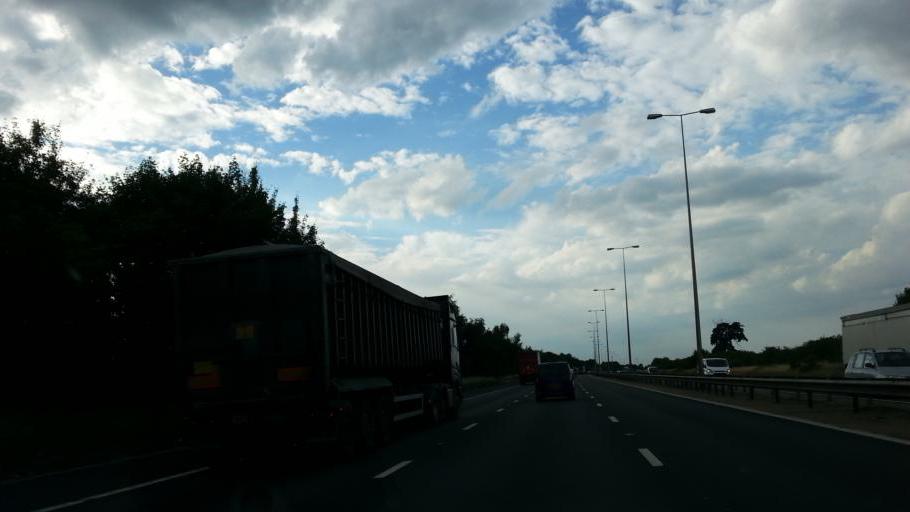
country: GB
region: England
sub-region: Worcestershire
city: Kempsey
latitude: 52.1104
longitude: -2.1944
